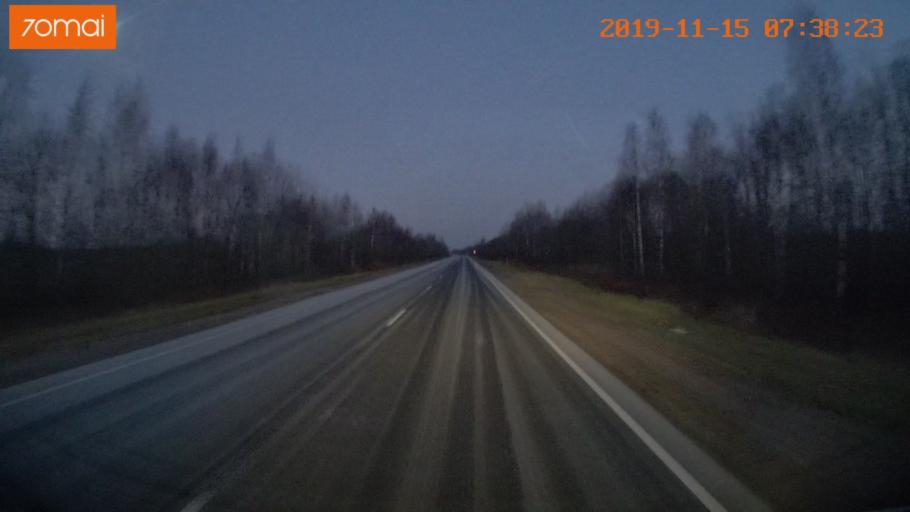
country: RU
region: Vologda
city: Sheksna
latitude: 58.7566
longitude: 38.4026
